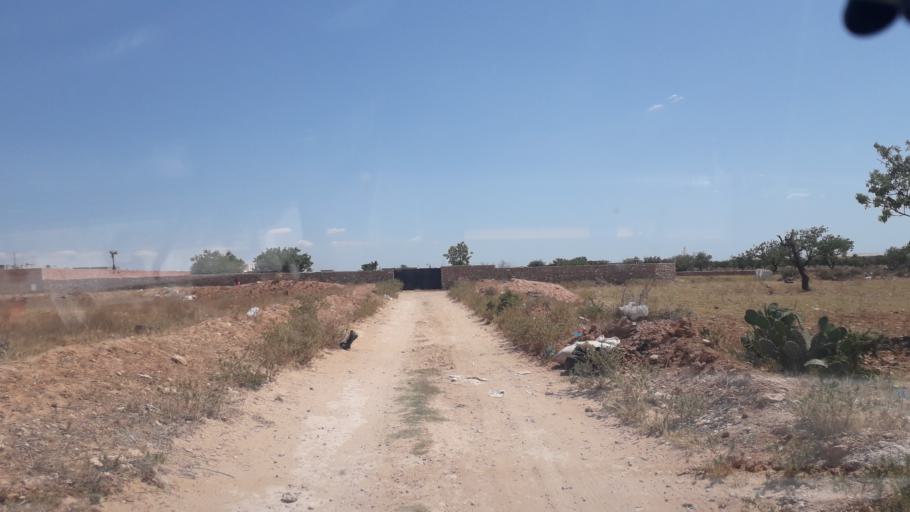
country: TN
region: Safaqis
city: Al Qarmadah
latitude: 34.8365
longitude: 10.7754
